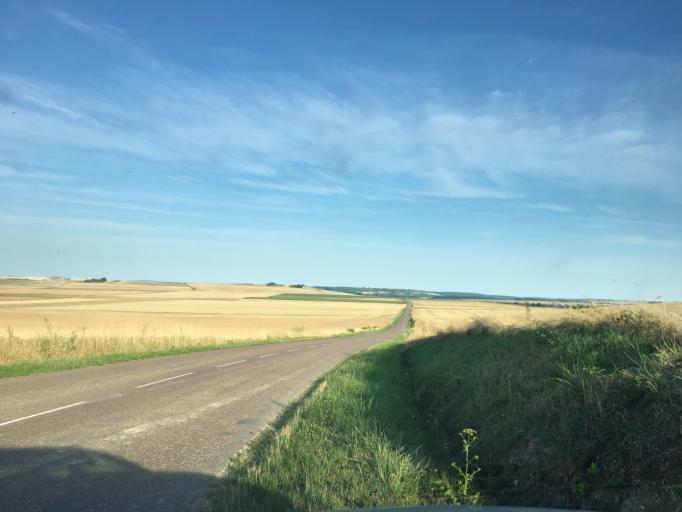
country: FR
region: Bourgogne
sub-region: Departement de l'Yonne
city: Aillant-sur-Tholon
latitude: 47.9059
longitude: 3.3869
